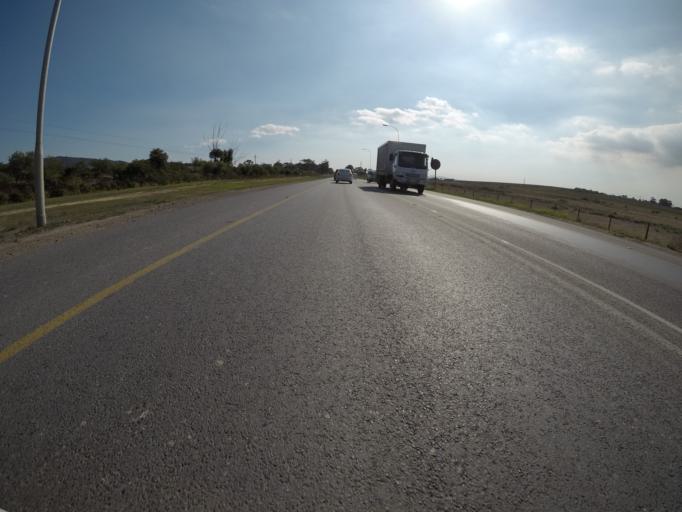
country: ZA
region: Western Cape
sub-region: Cape Winelands District Municipality
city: Stellenbosch
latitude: -33.8780
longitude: 18.8020
